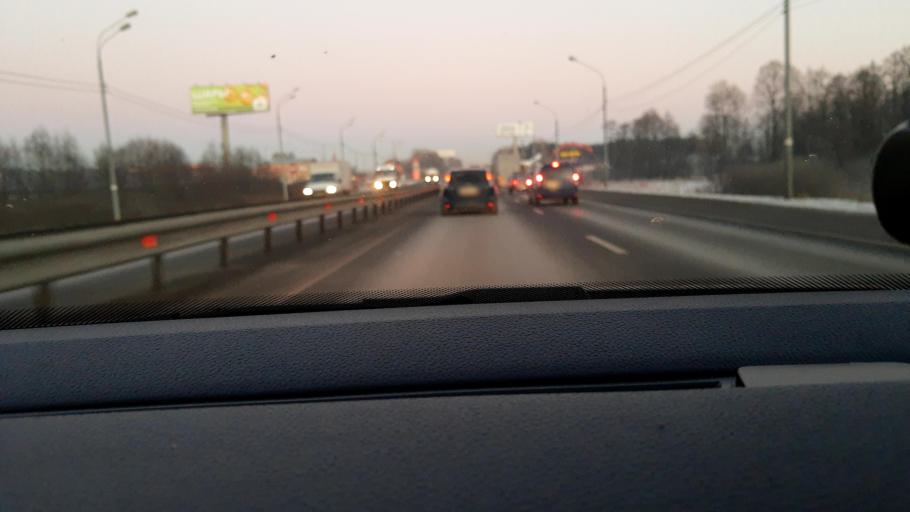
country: RU
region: Moskovskaya
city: Vishnyakovskiye Dachi
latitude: 55.8153
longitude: 38.1270
